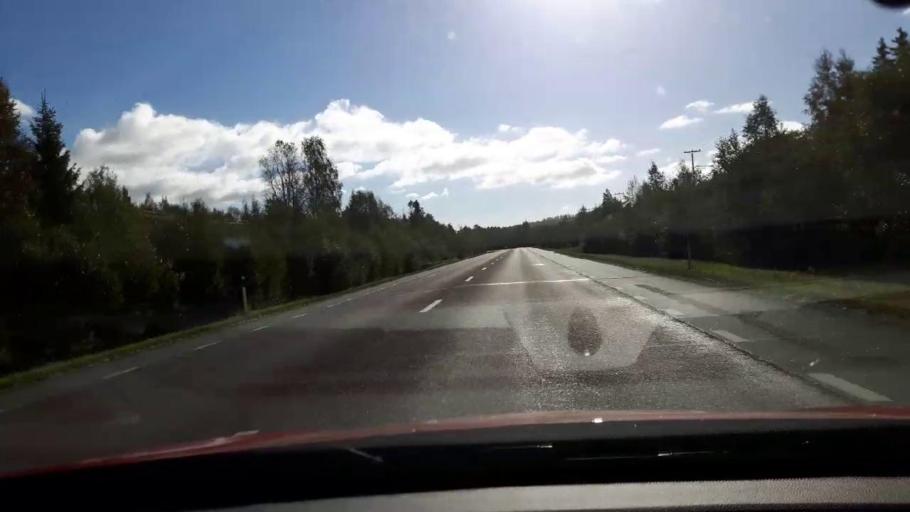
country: SE
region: Jaemtland
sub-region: Braecke Kommun
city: Braecke
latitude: 62.8174
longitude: 15.3401
